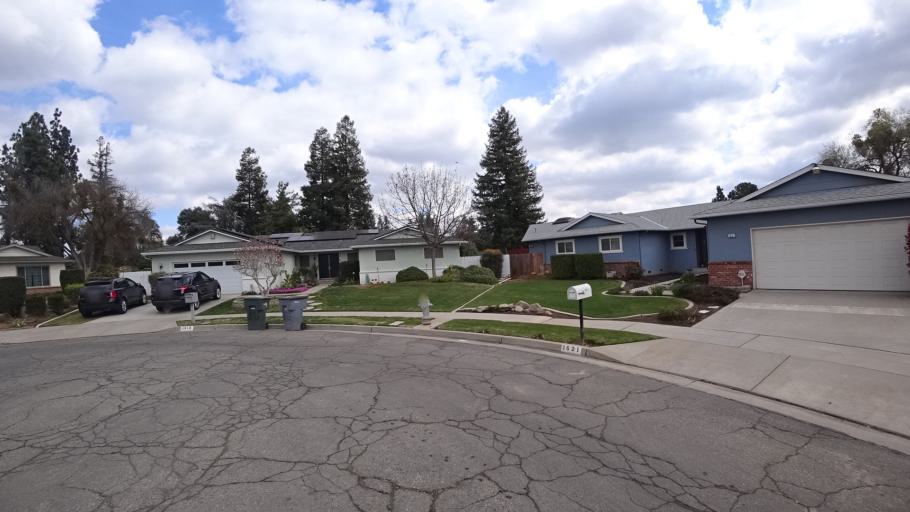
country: US
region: California
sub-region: Fresno County
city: Fresno
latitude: 36.8309
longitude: -119.8224
